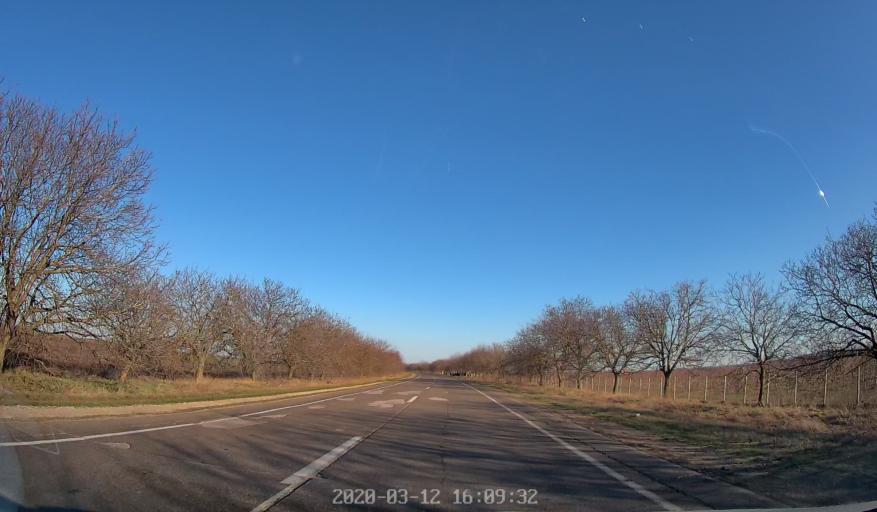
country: MD
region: Anenii Noi
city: Anenii Noi
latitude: 46.9566
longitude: 29.2215
